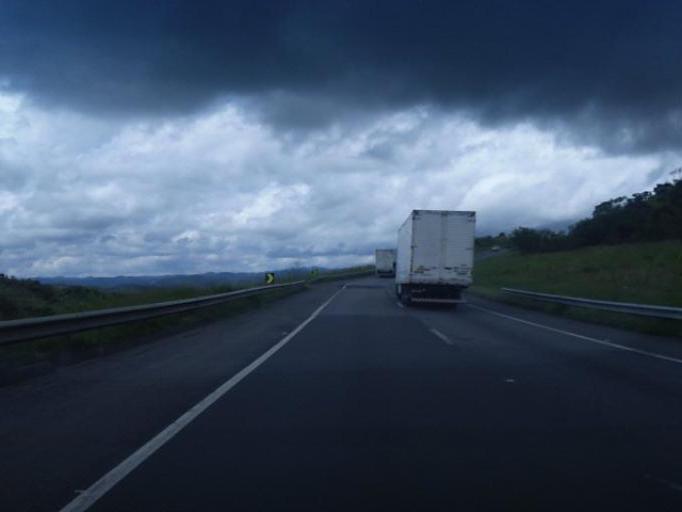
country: BR
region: Sao Paulo
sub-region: Cajati
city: Cajati
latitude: -24.9706
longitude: -48.4889
